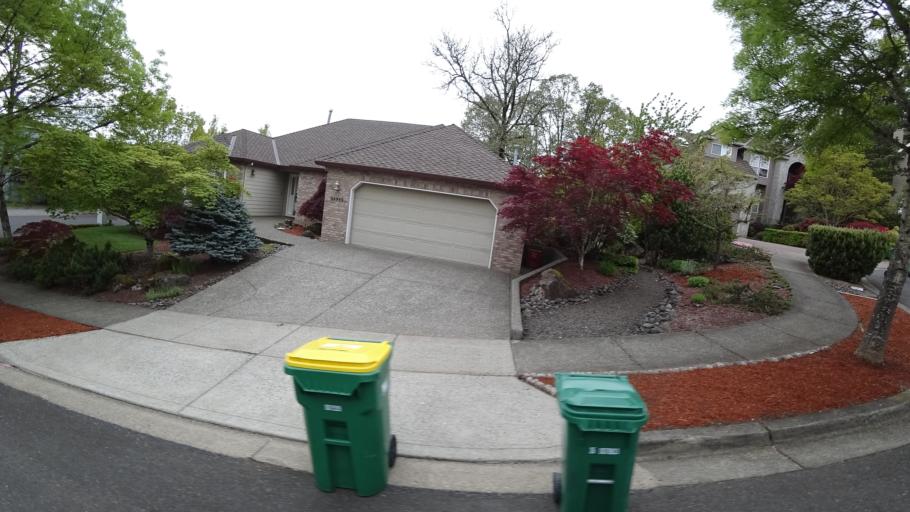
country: US
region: Oregon
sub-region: Washington County
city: Beaverton
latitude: 45.4561
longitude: -122.8313
